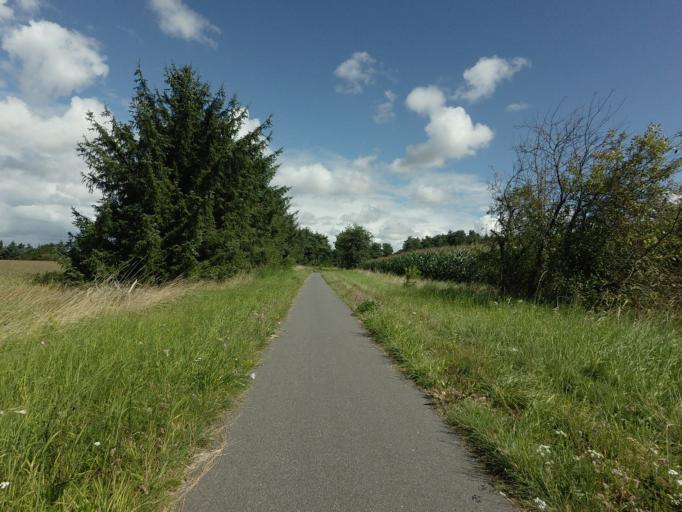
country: DK
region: Central Jutland
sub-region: Silkeborg Kommune
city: Svejbaek
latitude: 56.2082
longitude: 9.6718
